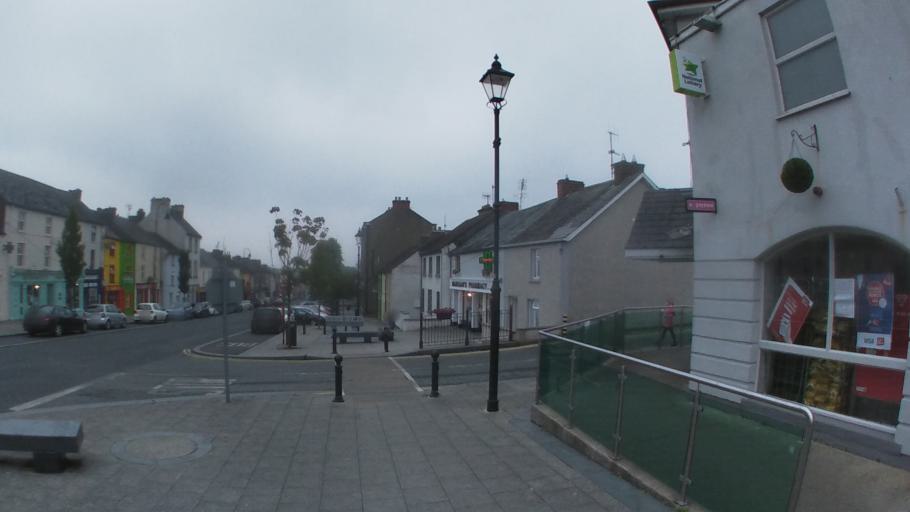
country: IE
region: Leinster
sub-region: Kilkenny
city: Callan
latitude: 52.5429
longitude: -7.3910
